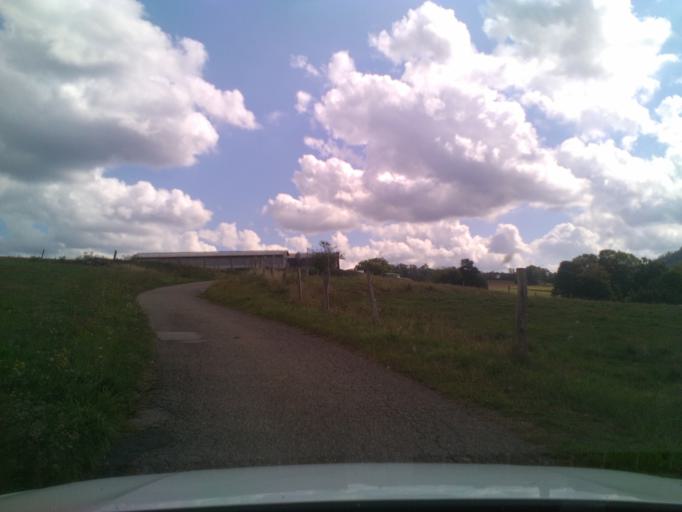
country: FR
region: Lorraine
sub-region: Departement des Vosges
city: Senones
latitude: 48.3968
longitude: 7.0027
